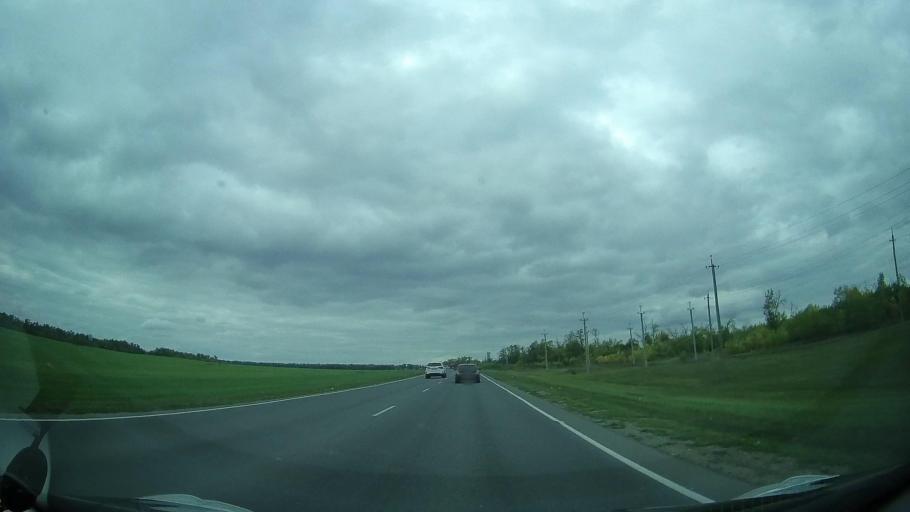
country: RU
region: Rostov
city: Yegorlykskaya
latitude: 46.5745
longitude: 40.6316
